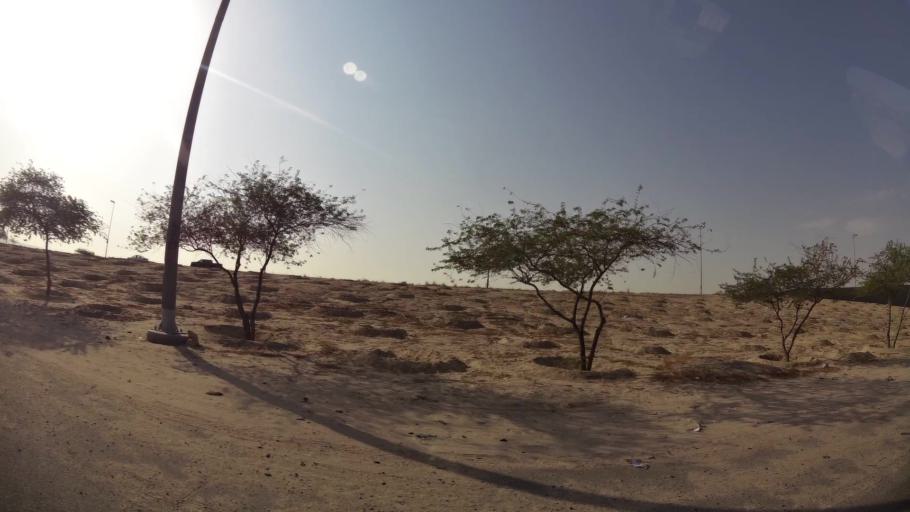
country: KW
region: Mubarak al Kabir
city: Mubarak al Kabir
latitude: 29.1789
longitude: 47.9983
